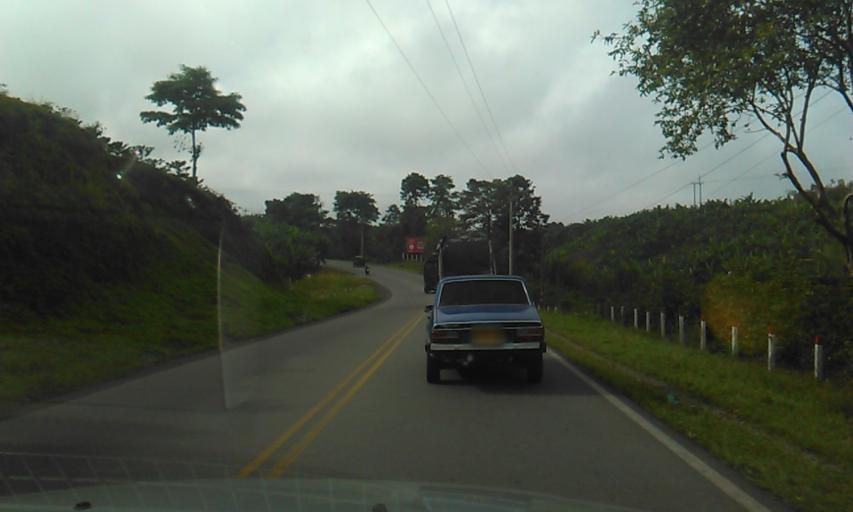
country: CO
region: Quindio
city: Cordoba
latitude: 4.4420
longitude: -75.7181
